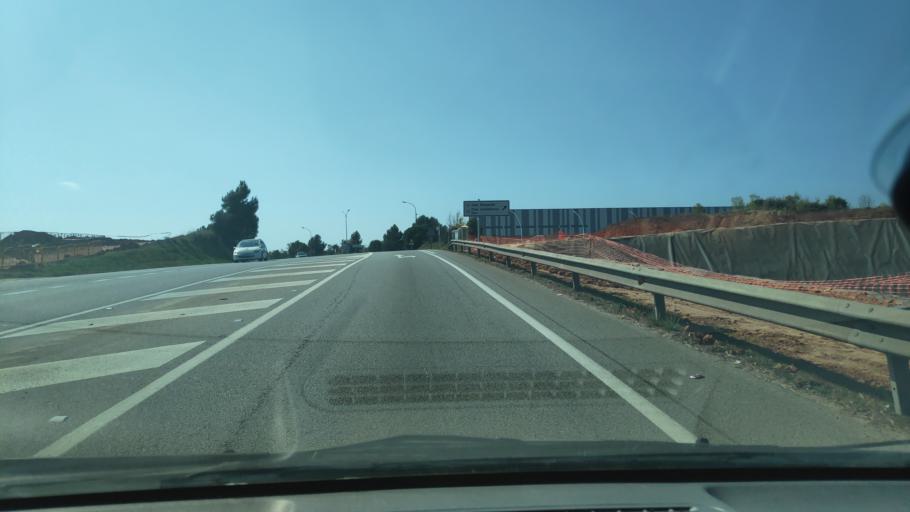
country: ES
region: Catalonia
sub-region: Provincia de Barcelona
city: Barbera del Valles
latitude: 41.5314
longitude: 2.1361
